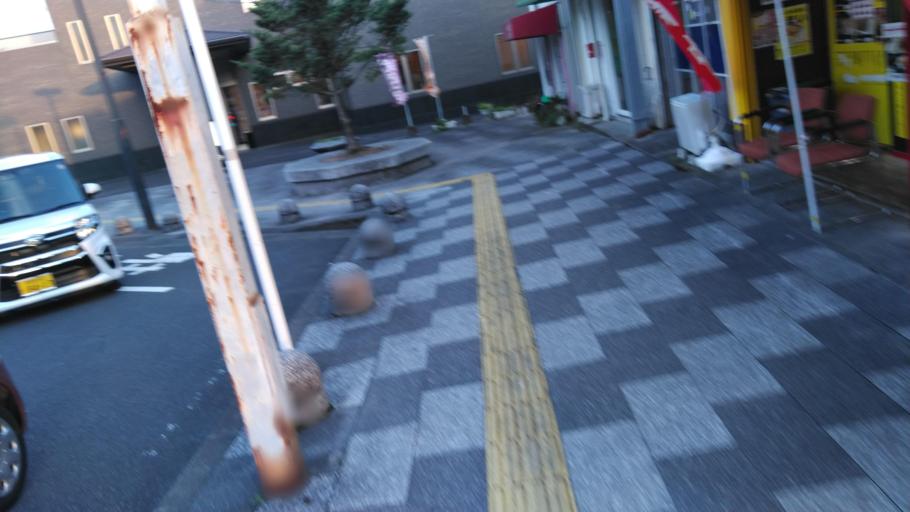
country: JP
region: Kagoshima
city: Kokubu-matsuki
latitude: 31.7433
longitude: 130.7634
